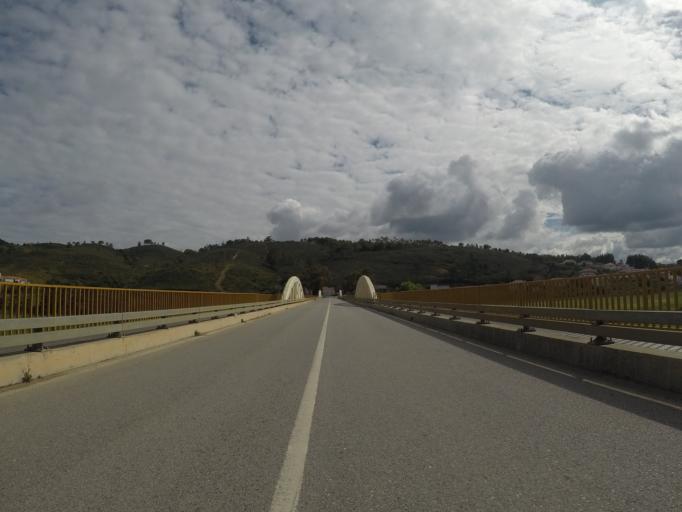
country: PT
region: Beja
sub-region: Odemira
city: Sao Teotonio
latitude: 37.4337
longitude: -8.7662
